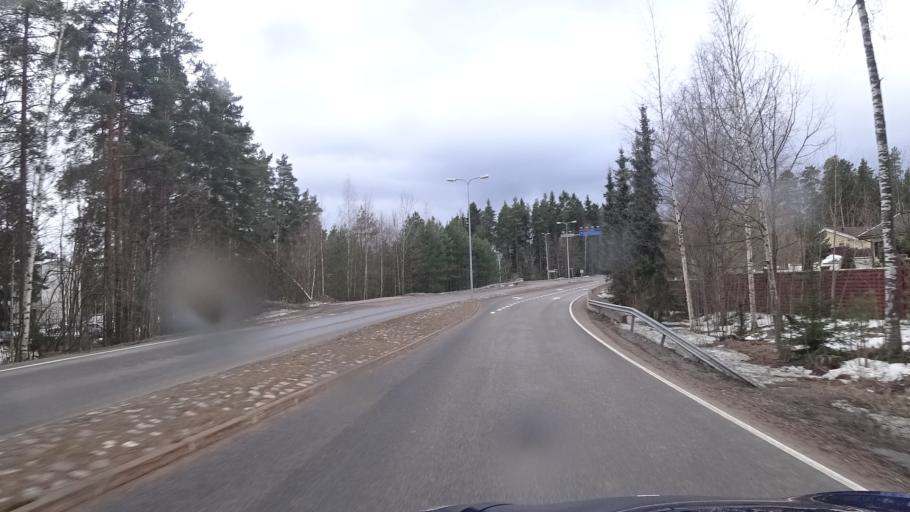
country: FI
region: Kymenlaakso
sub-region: Kotka-Hamina
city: Karhula
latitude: 60.5187
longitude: 26.8961
